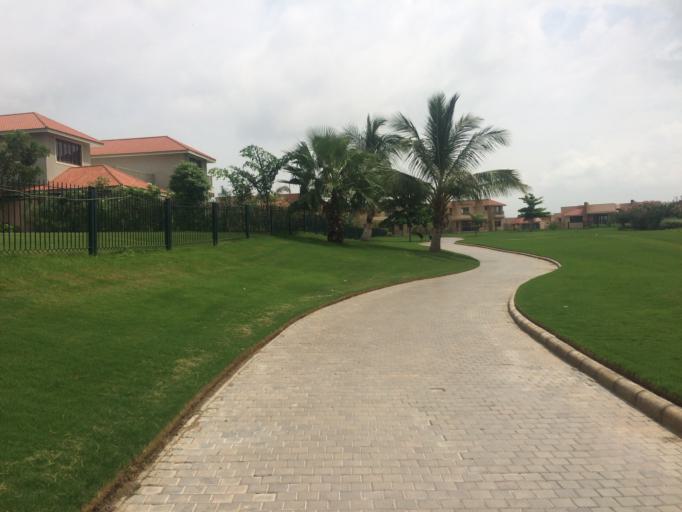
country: IN
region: Gujarat
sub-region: Ahmadabad
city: Sanand
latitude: 23.0210
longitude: 72.3599
